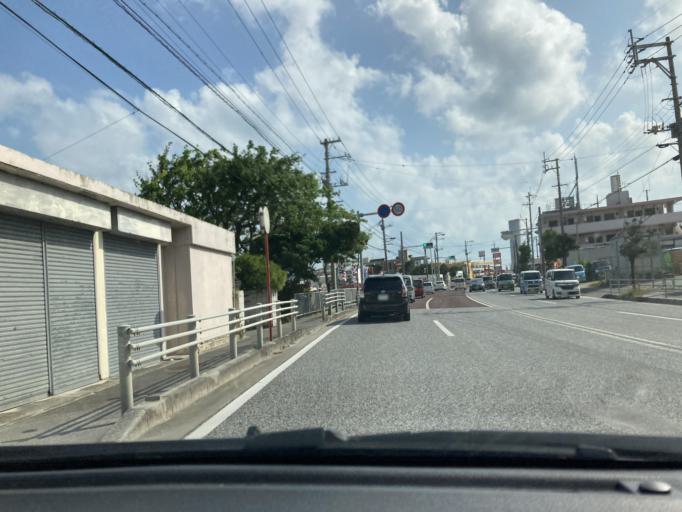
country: JP
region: Okinawa
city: Chatan
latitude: 26.2841
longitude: 127.8156
